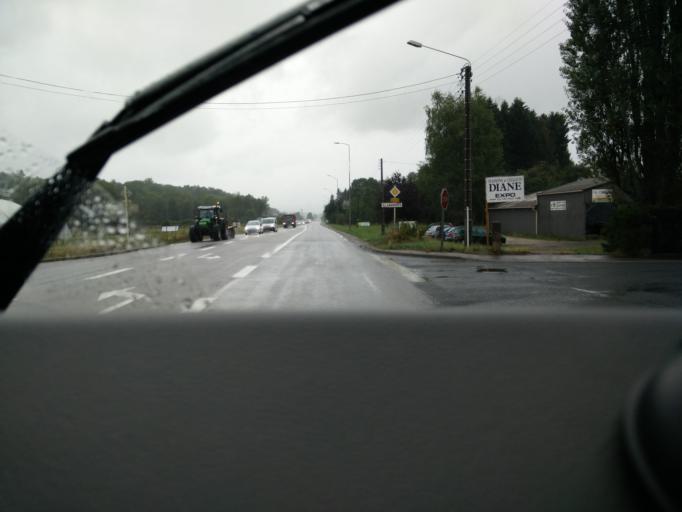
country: FR
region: Lorraine
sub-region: Departement des Vosges
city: Saint-Leonard
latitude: 48.2210
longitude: 6.9451
